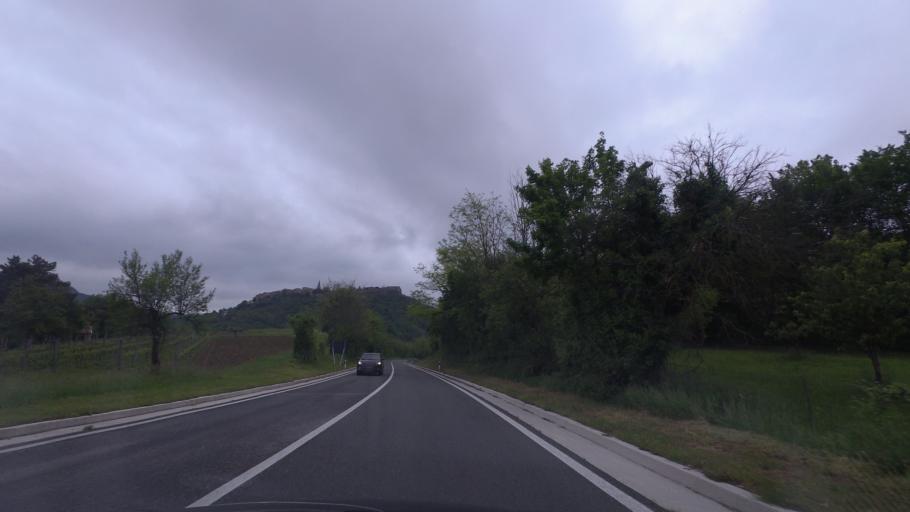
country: HR
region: Istarska
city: Buzet
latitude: 45.4065
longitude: 13.9790
